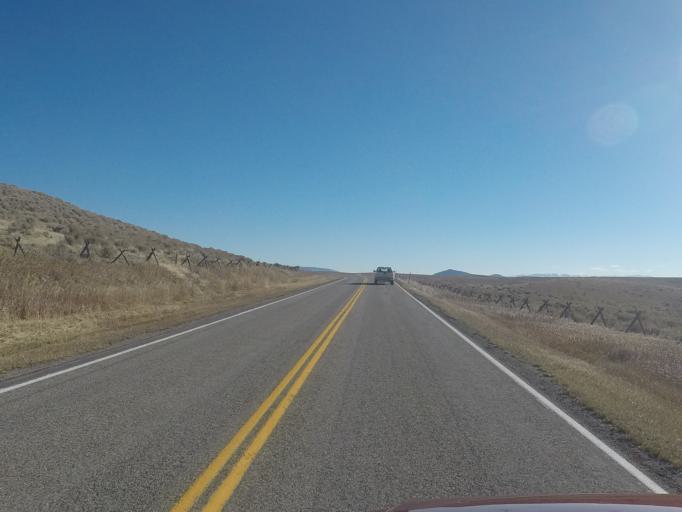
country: US
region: Montana
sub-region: Meagher County
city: White Sulphur Springs
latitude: 46.3552
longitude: -111.0260
